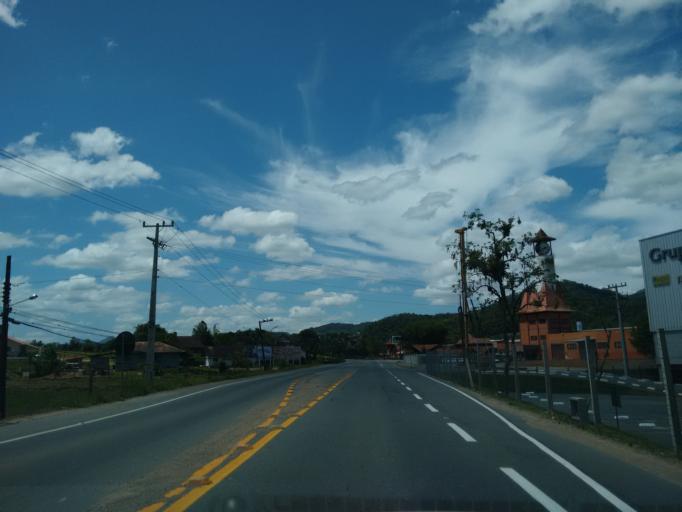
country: BR
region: Santa Catarina
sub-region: Pomerode
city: Pomerode
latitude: -26.7669
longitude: -49.1704
